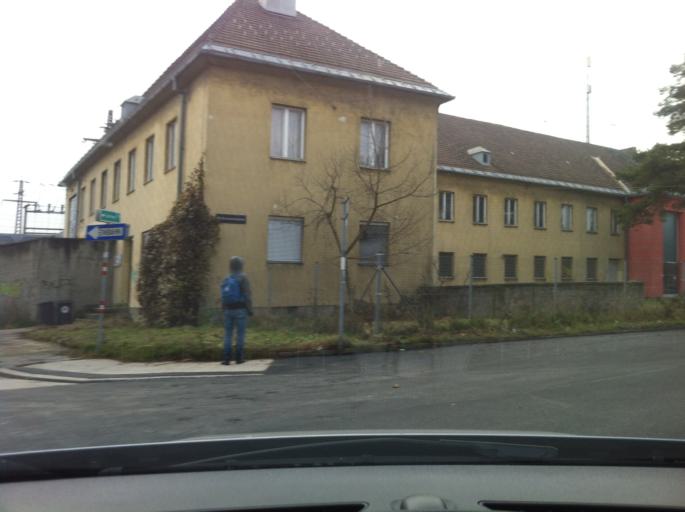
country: AT
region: Lower Austria
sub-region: Politischer Bezirk Modling
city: Perchtoldsdorf
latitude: 48.1955
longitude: 16.2724
